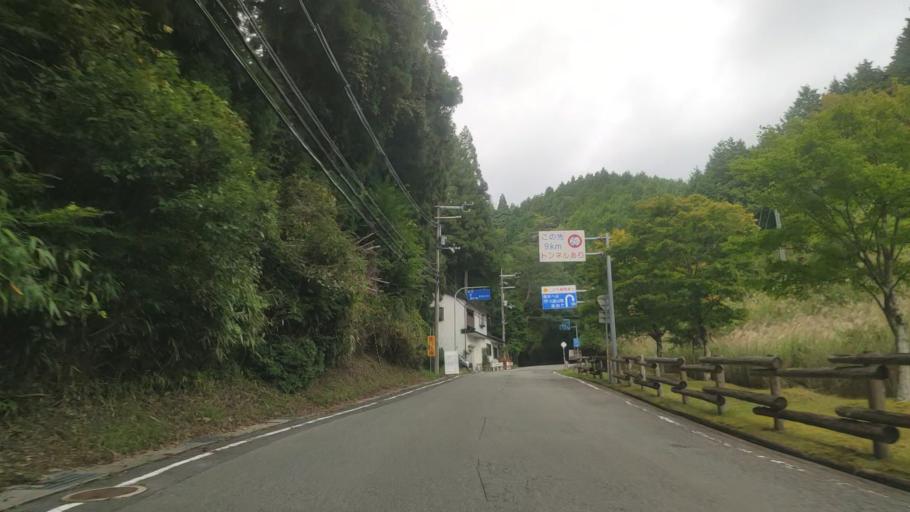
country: JP
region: Wakayama
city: Koya
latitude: 34.2184
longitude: 135.6116
